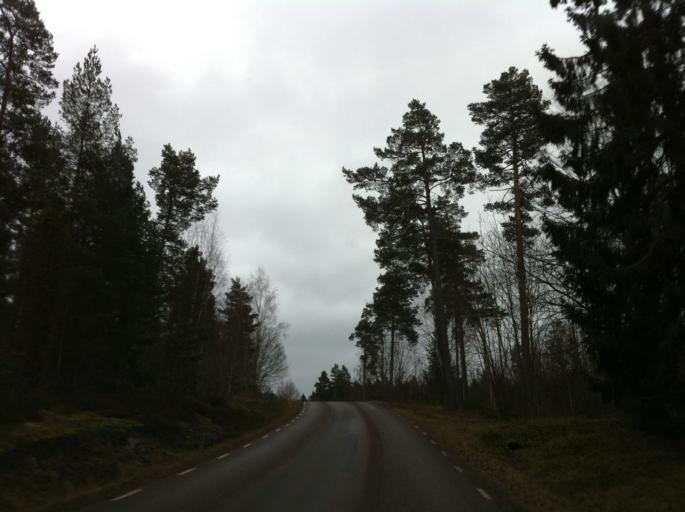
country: SE
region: Kalmar
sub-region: Vasterviks Kommun
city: Vaestervik
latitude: 57.9037
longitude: 16.6980
